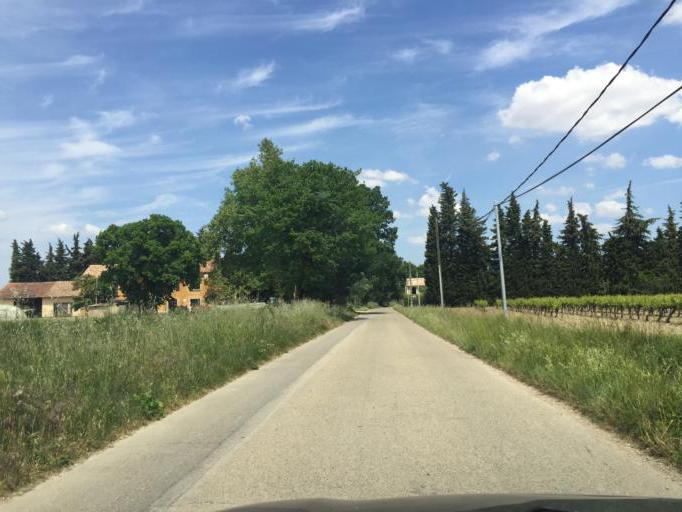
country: FR
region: Provence-Alpes-Cote d'Azur
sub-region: Departement du Vaucluse
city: Jonquieres
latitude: 44.1342
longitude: 4.9026
